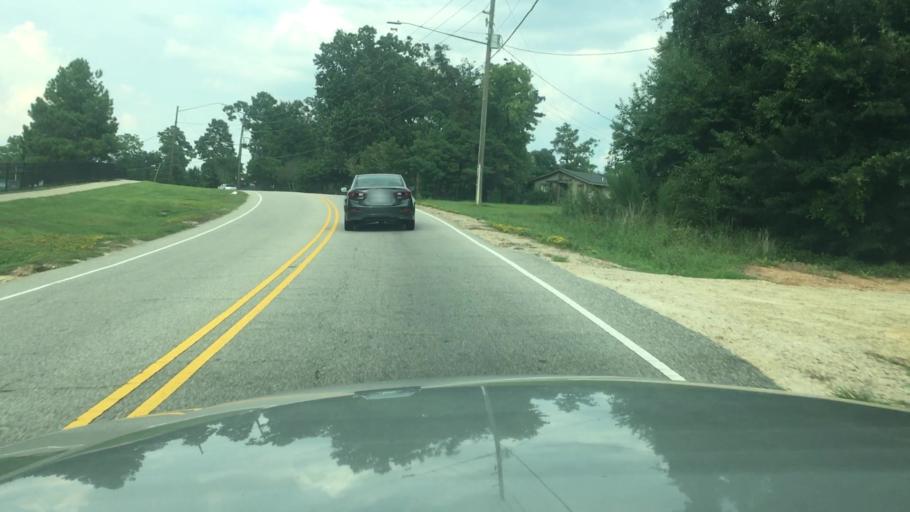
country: US
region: North Carolina
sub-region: Cumberland County
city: Fort Bragg
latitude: 35.1030
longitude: -78.9984
